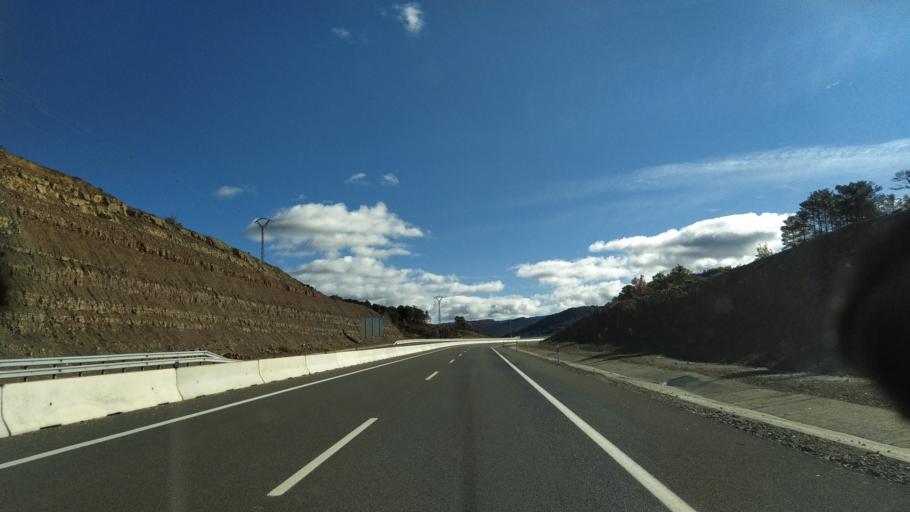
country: ES
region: Aragon
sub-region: Provincia de Huesca
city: Arguis
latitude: 42.4057
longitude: -0.3798
